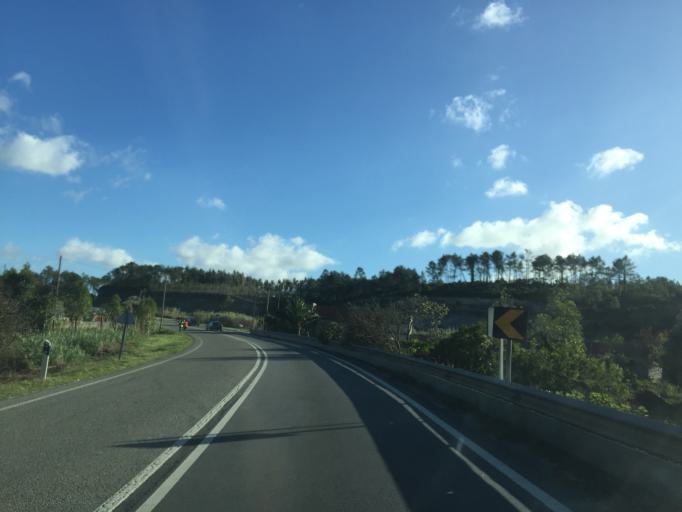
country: PT
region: Coimbra
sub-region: Figueira da Foz
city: Tavarede
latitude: 40.1948
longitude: -8.8330
